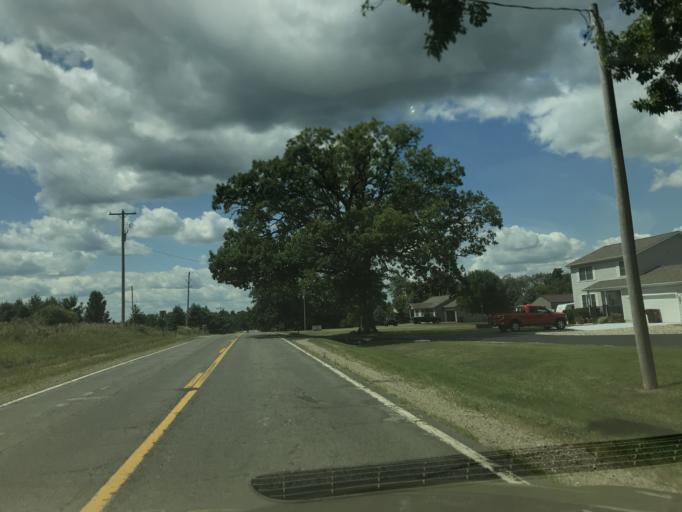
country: US
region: Michigan
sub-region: Eaton County
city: Eaton Rapids
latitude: 42.4511
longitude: -84.5533
